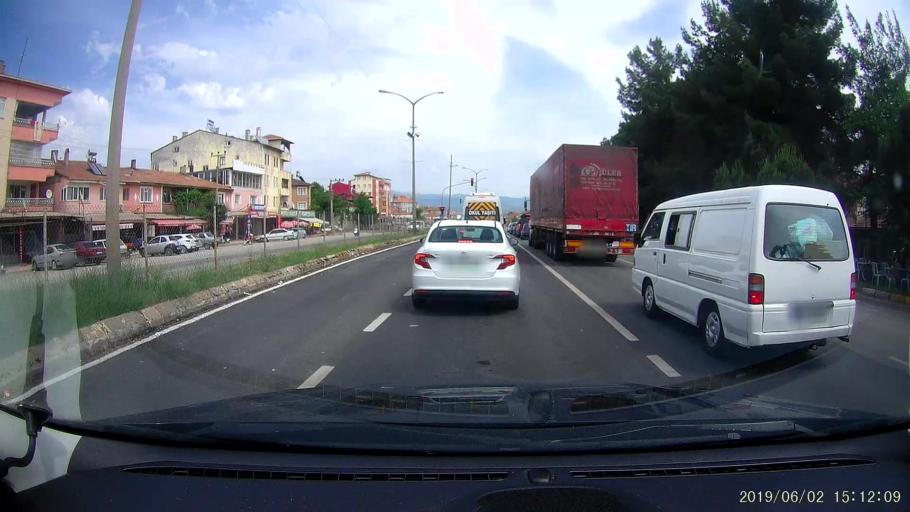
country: TR
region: Corum
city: Osmancik
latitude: 40.9769
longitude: 34.8106
